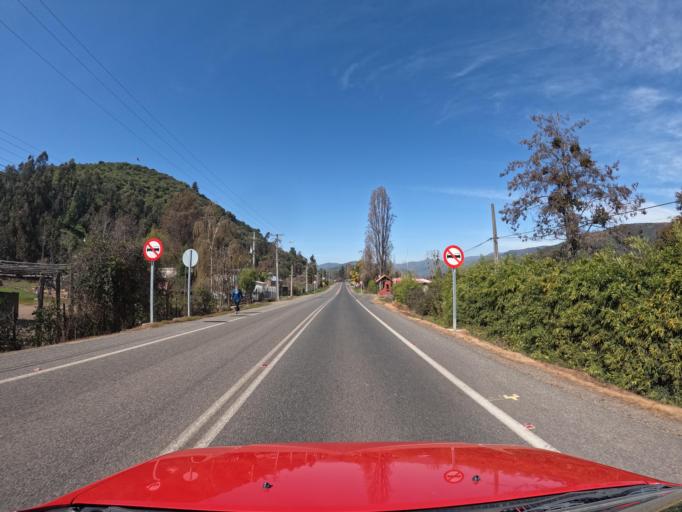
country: CL
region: Maule
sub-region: Provincia de Curico
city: Teno
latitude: -34.9783
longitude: -70.9852
